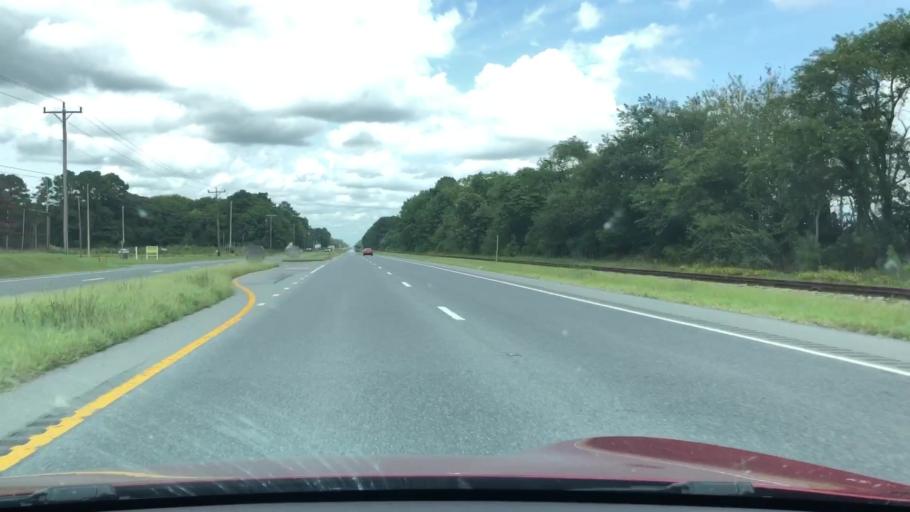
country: US
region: Virginia
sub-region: Northampton County
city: Exmore
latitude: 37.5984
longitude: -75.7766
